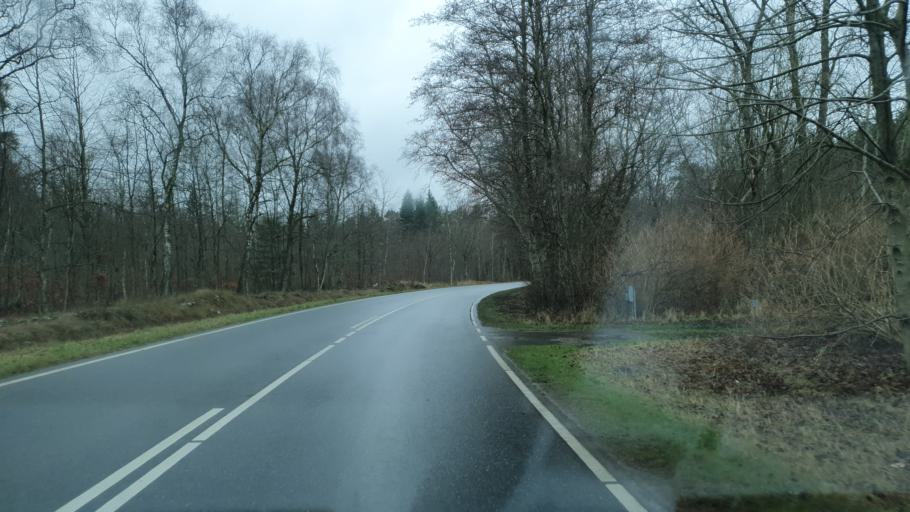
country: DK
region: North Denmark
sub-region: Jammerbugt Kommune
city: Fjerritslev
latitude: 57.1187
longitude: 9.1259
